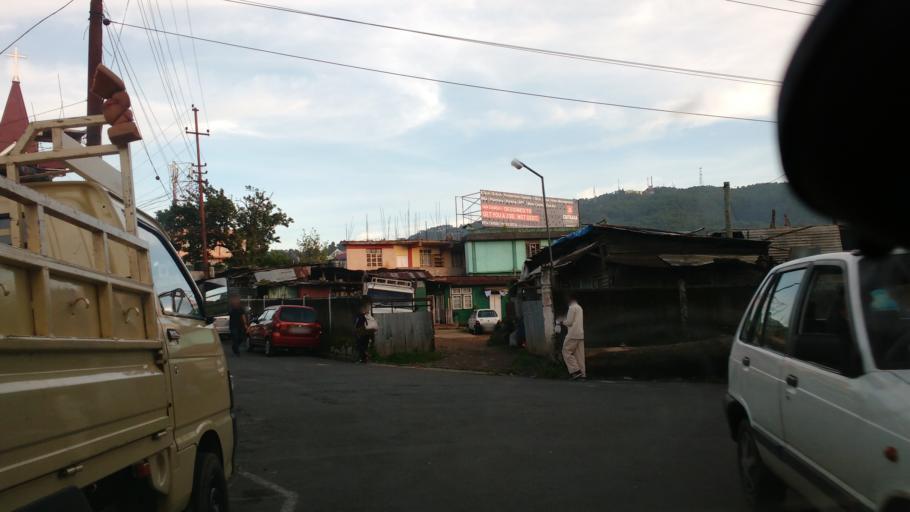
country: IN
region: Meghalaya
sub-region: East Khasi Hills
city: Shillong
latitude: 25.5648
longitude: 91.9034
